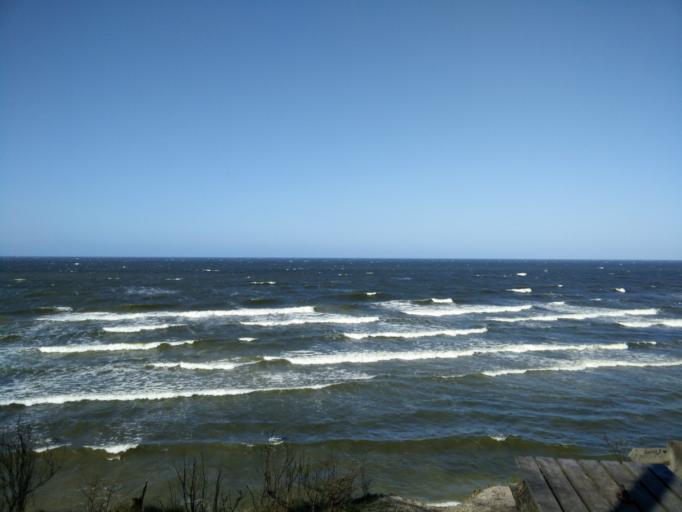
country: LT
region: Klaipedos apskritis
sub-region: Klaipeda
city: Klaipeda
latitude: 55.7958
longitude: 21.0681
